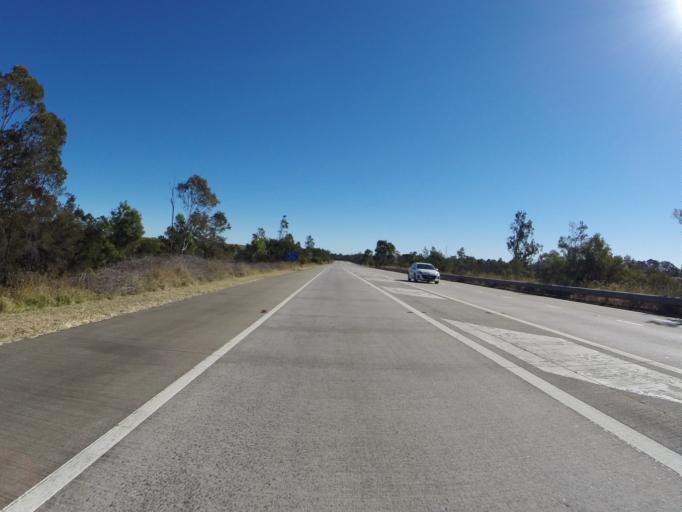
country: AU
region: New South Wales
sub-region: Wollondilly
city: Douglas Park
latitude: -34.2445
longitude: 150.6983
